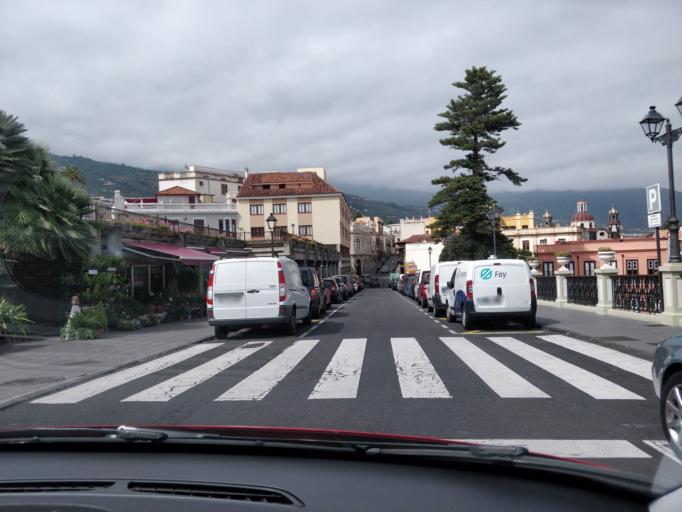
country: ES
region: Canary Islands
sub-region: Provincia de Santa Cruz de Tenerife
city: La Orotava
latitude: 28.3911
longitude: -16.5231
